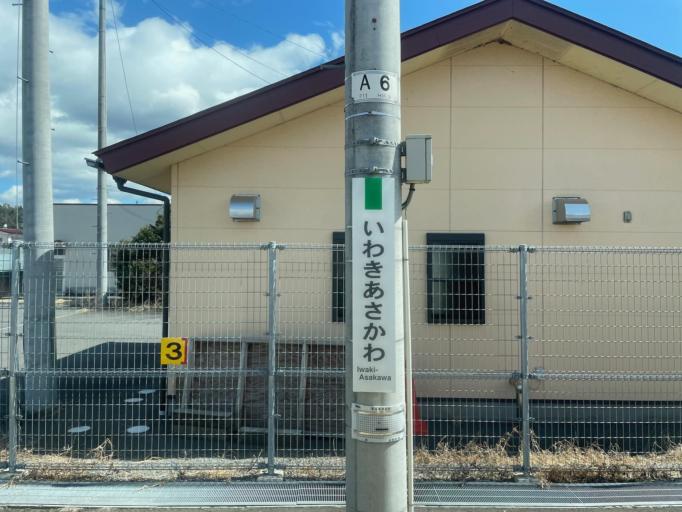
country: JP
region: Fukushima
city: Ishikawa
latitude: 37.0799
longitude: 140.4145
